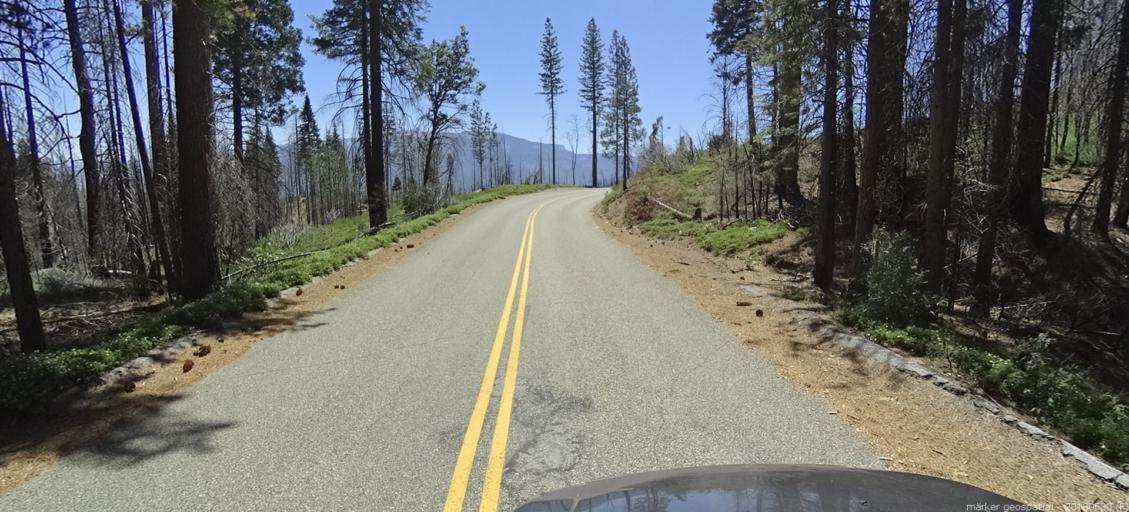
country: US
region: California
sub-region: Fresno County
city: Auberry
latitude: 37.3321
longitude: -119.3682
